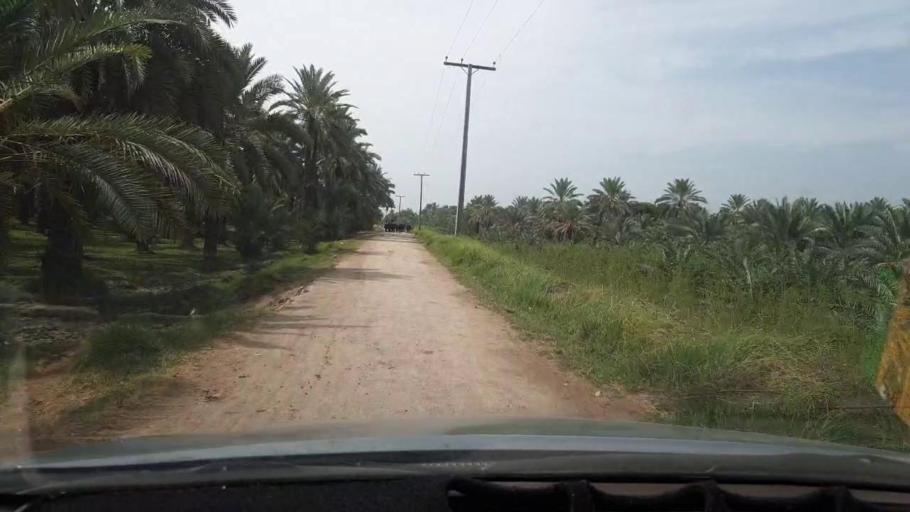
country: PK
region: Sindh
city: Khairpur
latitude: 27.4970
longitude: 68.7545
